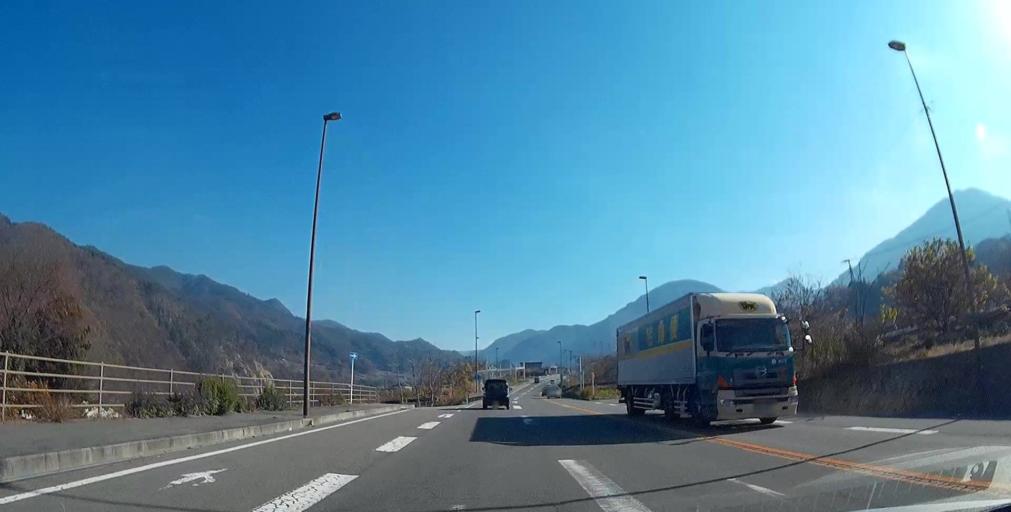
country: JP
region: Yamanashi
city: Isawa
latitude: 35.6114
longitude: 138.6989
